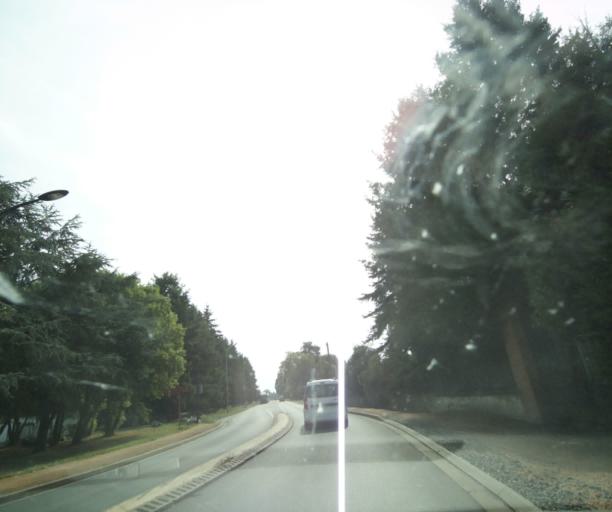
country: FR
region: Auvergne
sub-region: Departement de l'Allier
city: Bellerive-sur-Allier
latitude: 46.1340
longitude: 3.3998
